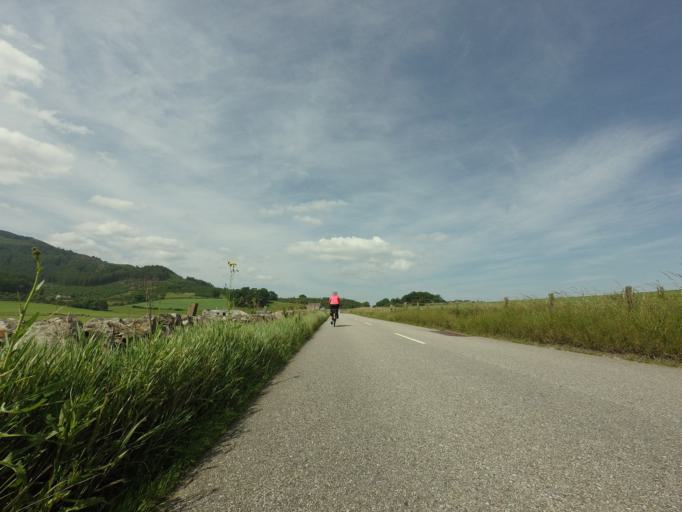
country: GB
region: Scotland
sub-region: Highland
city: Tain
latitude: 57.8472
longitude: -4.2007
